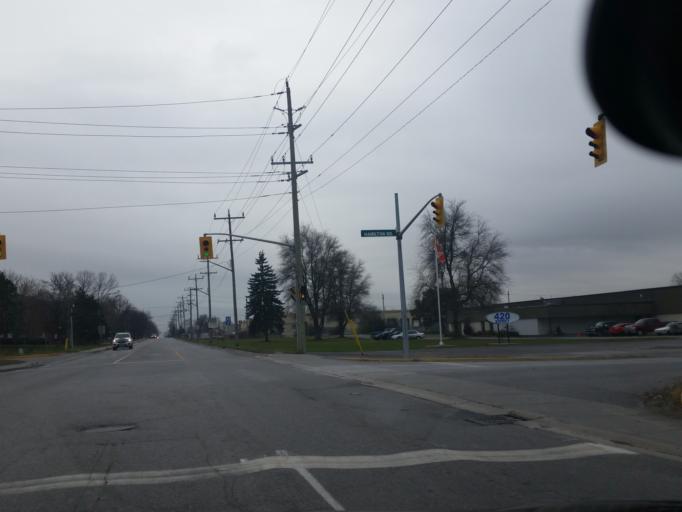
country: CA
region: Ontario
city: Quinte West
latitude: 44.1268
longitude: -77.5801
